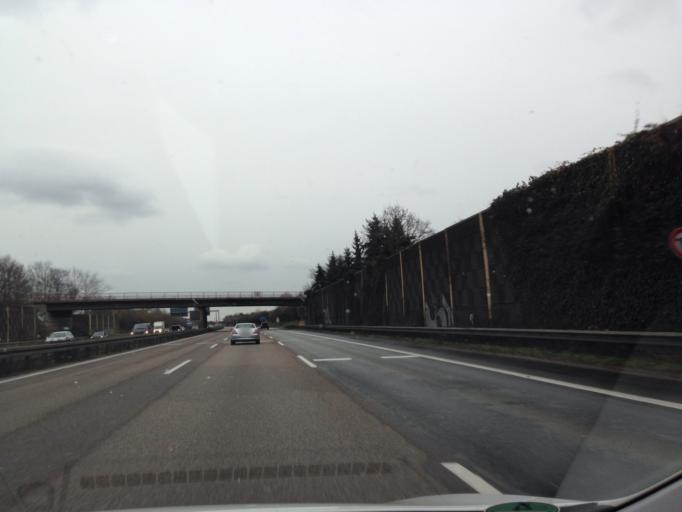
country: DE
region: North Rhine-Westphalia
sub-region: Regierungsbezirk Dusseldorf
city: Moers
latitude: 51.4357
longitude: 6.6314
